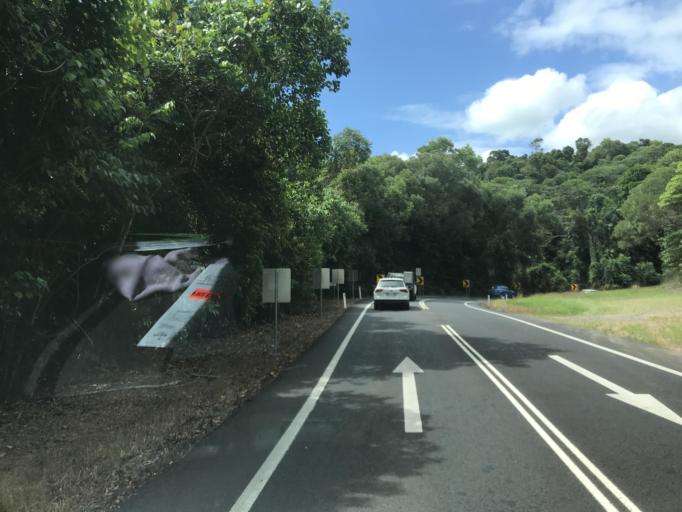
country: AU
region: Queensland
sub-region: Cassowary Coast
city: Innisfail
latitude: -17.8663
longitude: 146.0748
